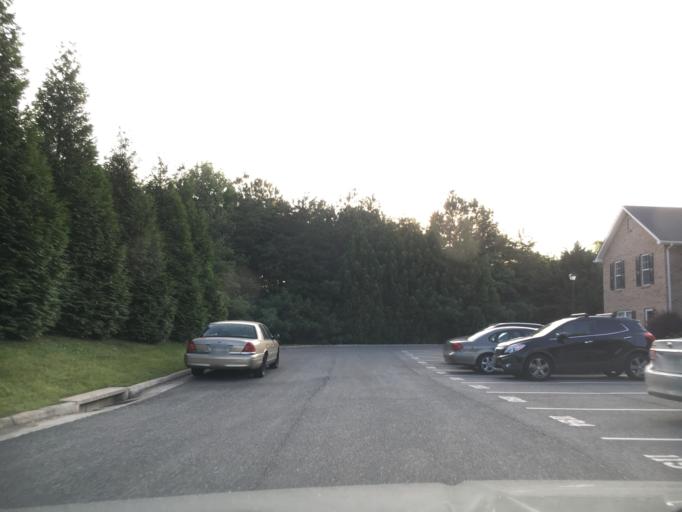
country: US
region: Virginia
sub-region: Bedford County
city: Forest
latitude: 37.3669
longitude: -79.3073
